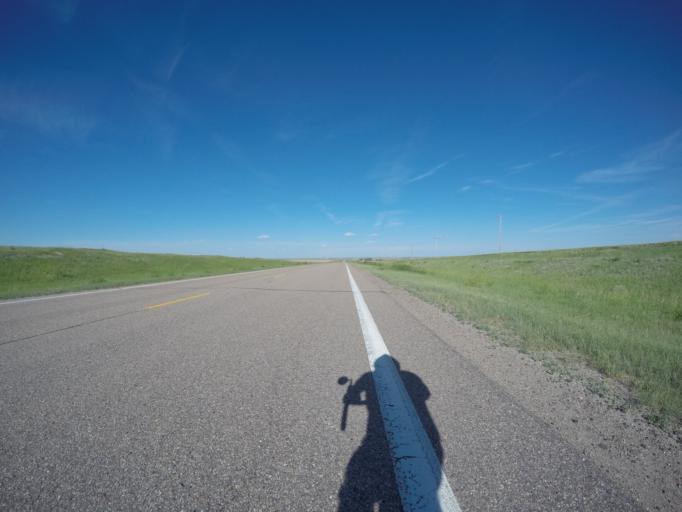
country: US
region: Kansas
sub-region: Cheyenne County
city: Saint Francis
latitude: 39.7567
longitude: -101.9436
